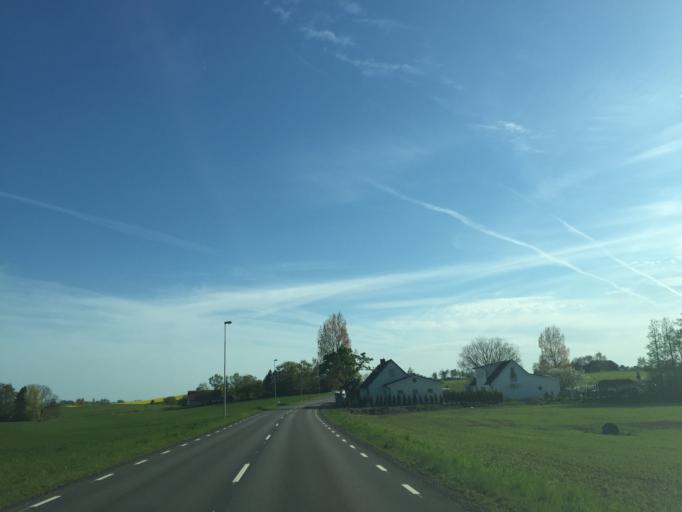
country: SE
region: Skane
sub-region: Malmo
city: Oxie
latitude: 55.5683
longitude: 13.1160
